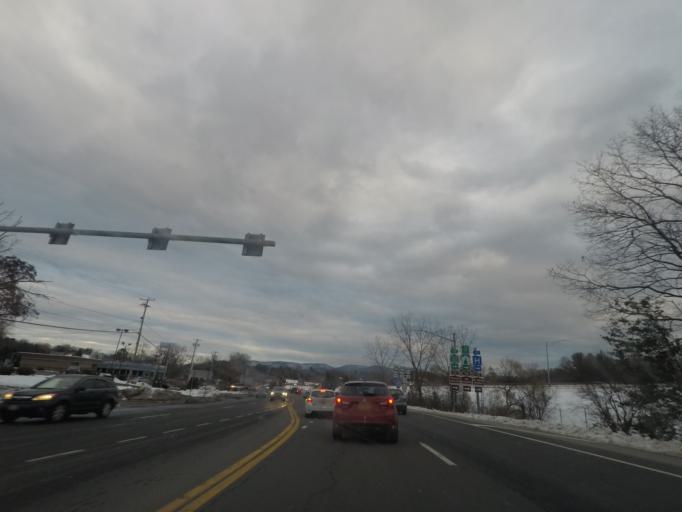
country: US
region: New York
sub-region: Orange County
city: Balmville
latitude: 41.5207
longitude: -74.0239
